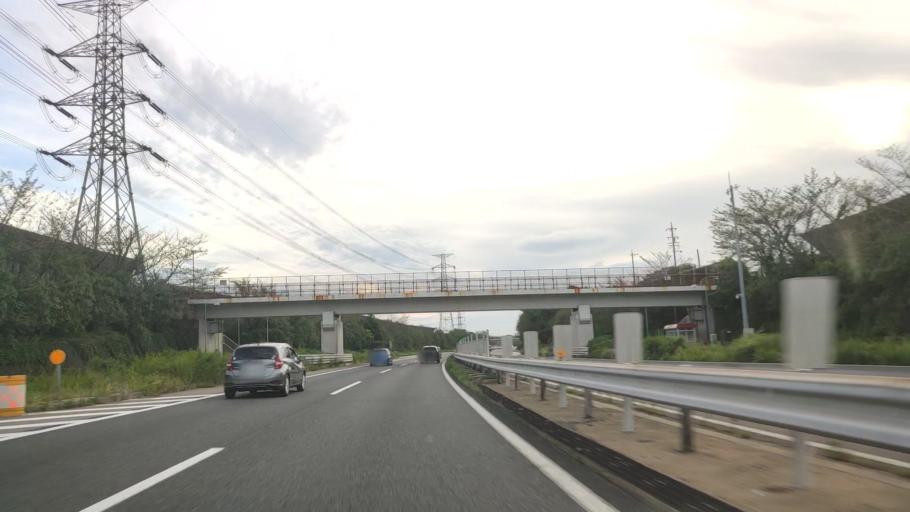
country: JP
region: Aichi
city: Kasugai
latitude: 35.2980
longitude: 136.9925
